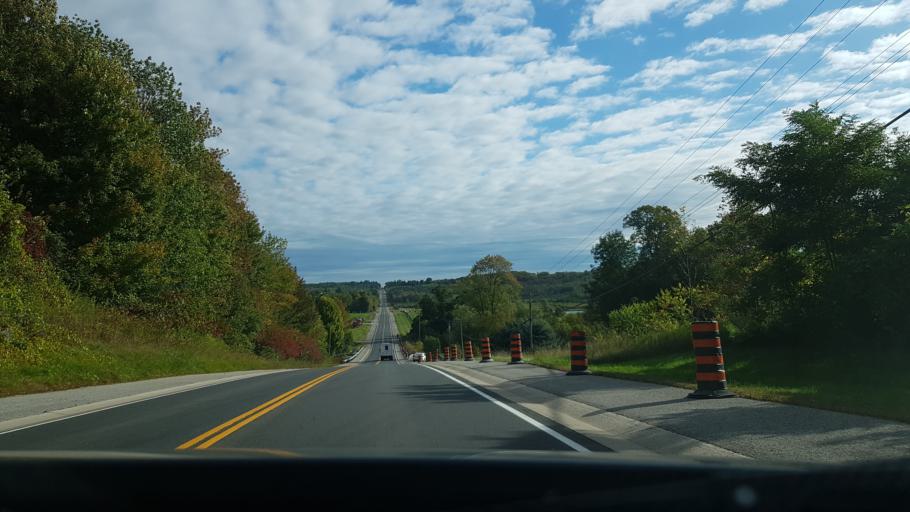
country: CA
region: Ontario
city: Orillia
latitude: 44.5978
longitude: -79.5656
